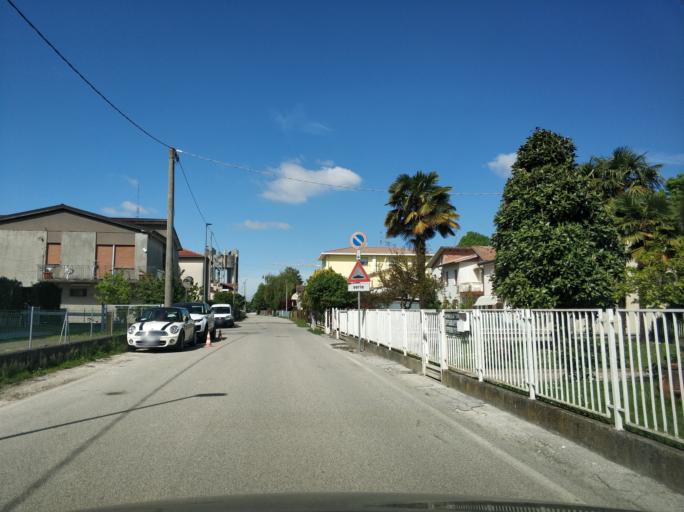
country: IT
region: Veneto
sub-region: Provincia di Venezia
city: Fiesso d'Artico
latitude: 45.4190
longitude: 12.0277
